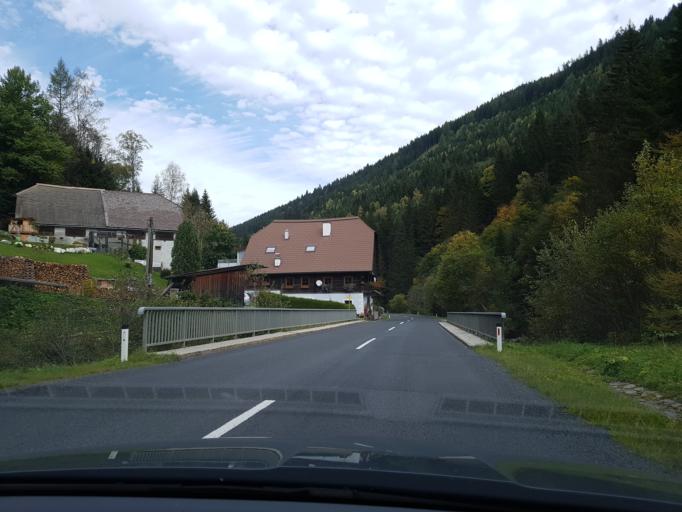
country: AT
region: Salzburg
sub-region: Politischer Bezirk Tamsweg
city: Ramingstein
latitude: 47.0325
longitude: 13.9038
